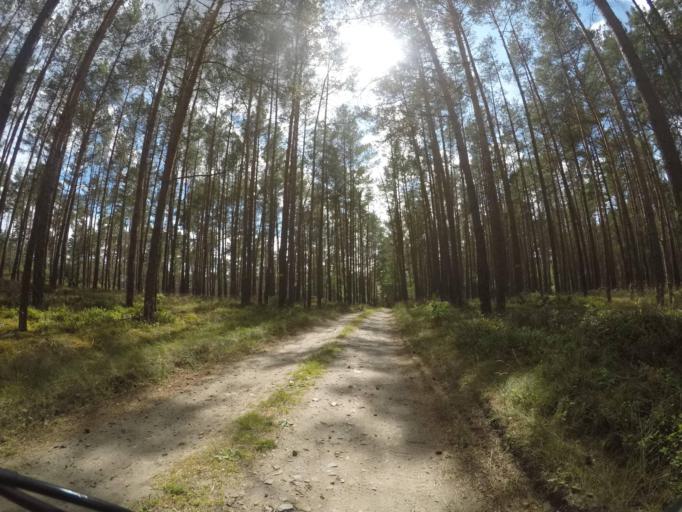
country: DE
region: Mecklenburg-Vorpommern
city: Lubtheen
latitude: 53.2583
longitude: 10.9923
